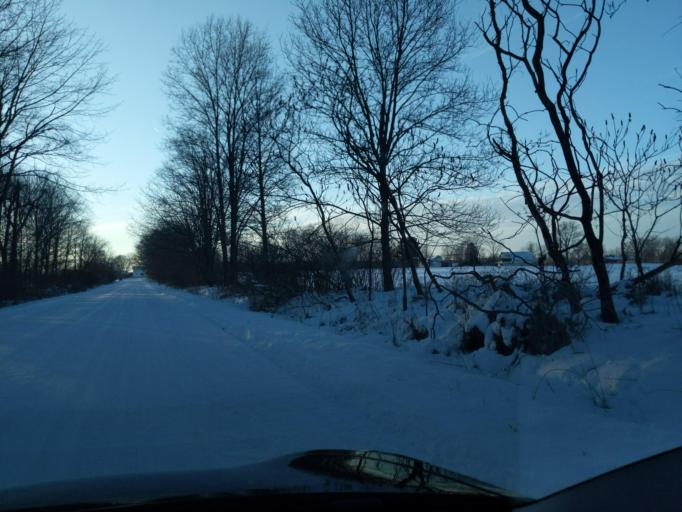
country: US
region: Michigan
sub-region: Ingham County
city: Webberville
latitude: 42.5679
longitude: -84.1391
